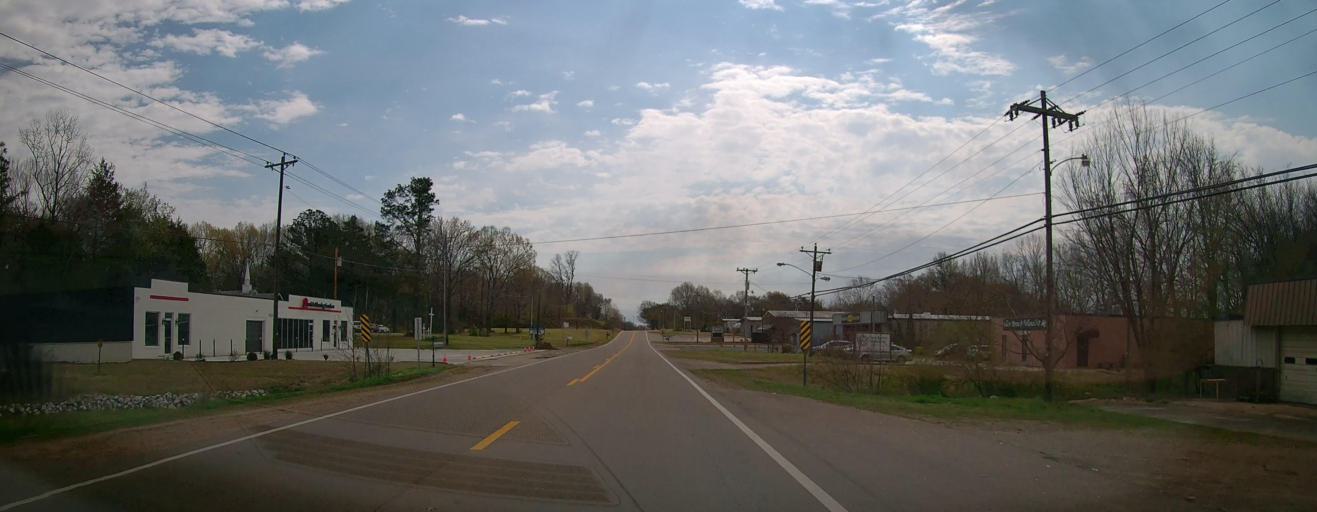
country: US
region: Mississippi
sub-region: De Soto County
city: Olive Branch
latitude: 34.9746
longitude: -89.8443
